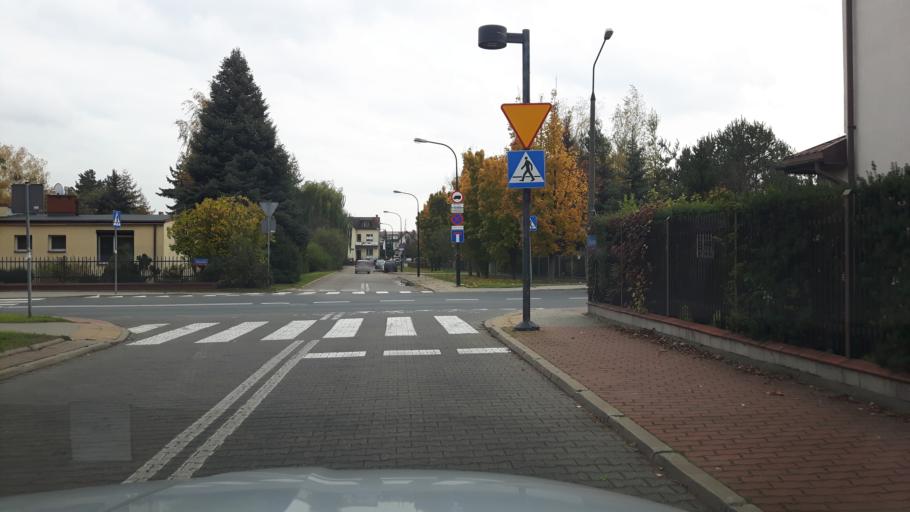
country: PL
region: Masovian Voivodeship
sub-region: Warszawa
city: Targowek
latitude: 52.2845
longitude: 21.0586
